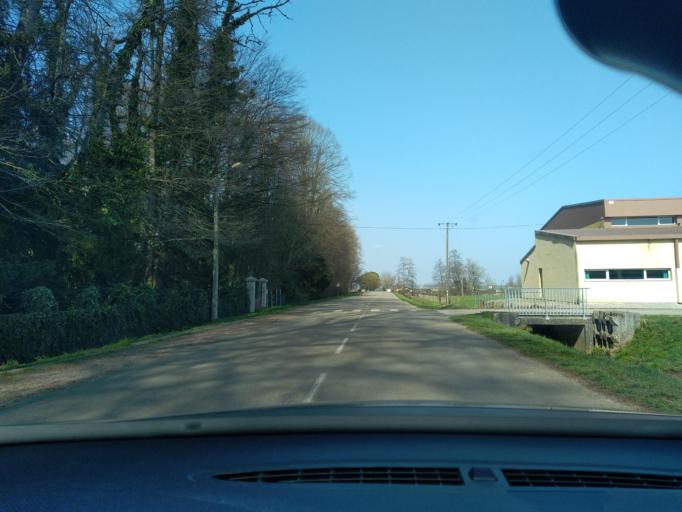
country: FR
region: Franche-Comte
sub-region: Departement du Jura
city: Mont-sous-Vaudrey
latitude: 46.9828
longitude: 5.6050
